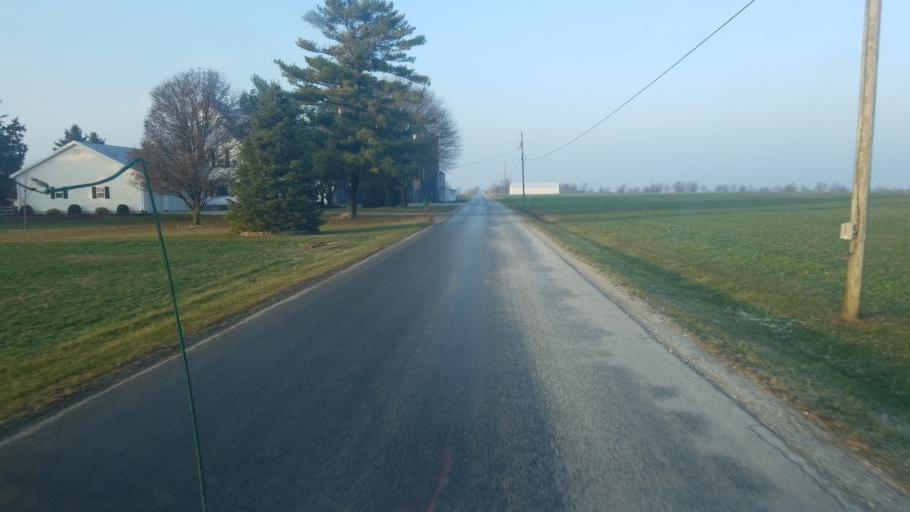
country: US
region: Ohio
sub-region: Wyandot County
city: Carey
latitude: 40.9668
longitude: -83.4061
